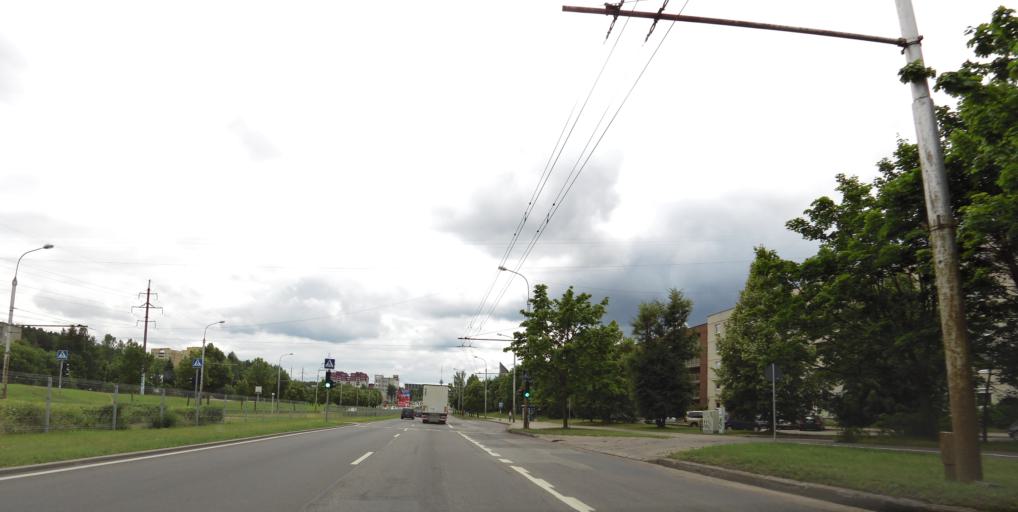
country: LT
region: Vilnius County
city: Justiniskes
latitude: 54.7197
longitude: 25.2325
